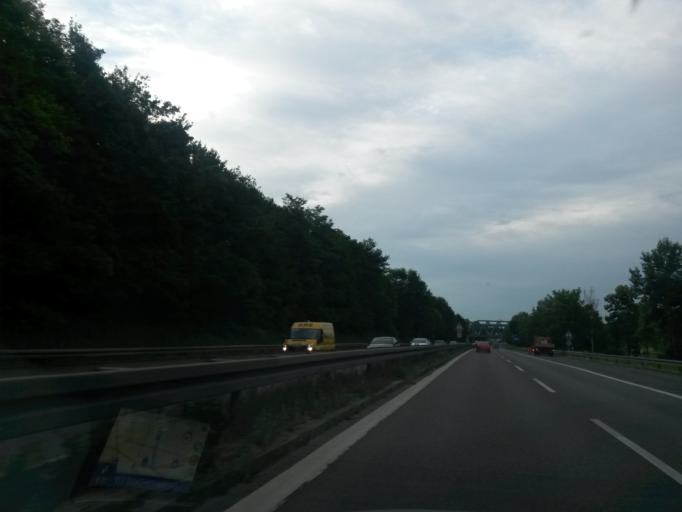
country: DE
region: Bavaria
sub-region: Regierungsbezirk Mittelfranken
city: Grossreuth bei Schweinau
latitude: 49.4207
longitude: 11.0455
